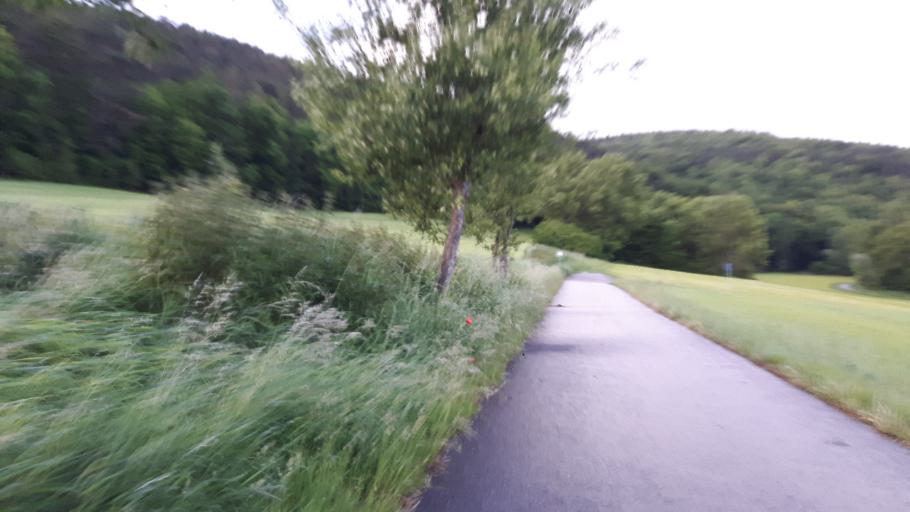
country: DE
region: Thuringia
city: Hetschburg
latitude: 50.9161
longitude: 11.3097
